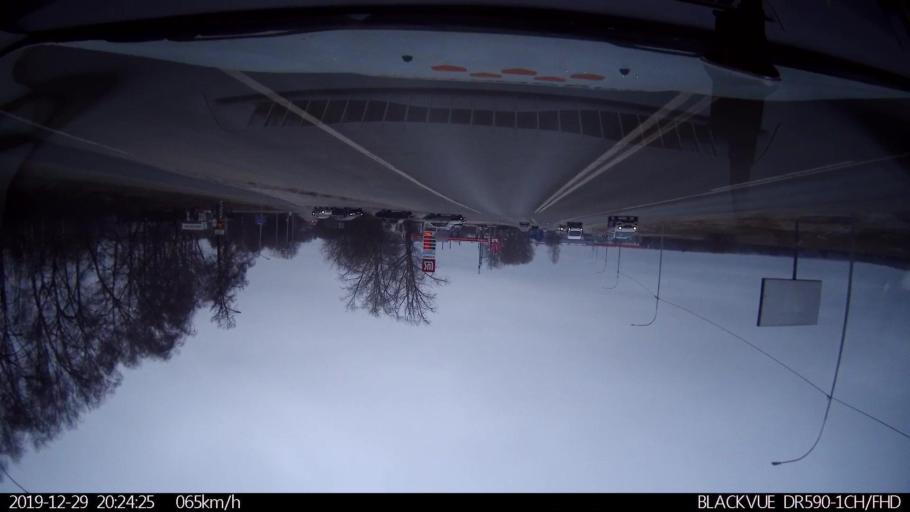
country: RU
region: Nizjnij Novgorod
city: Afonino
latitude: 56.2149
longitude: 44.1057
